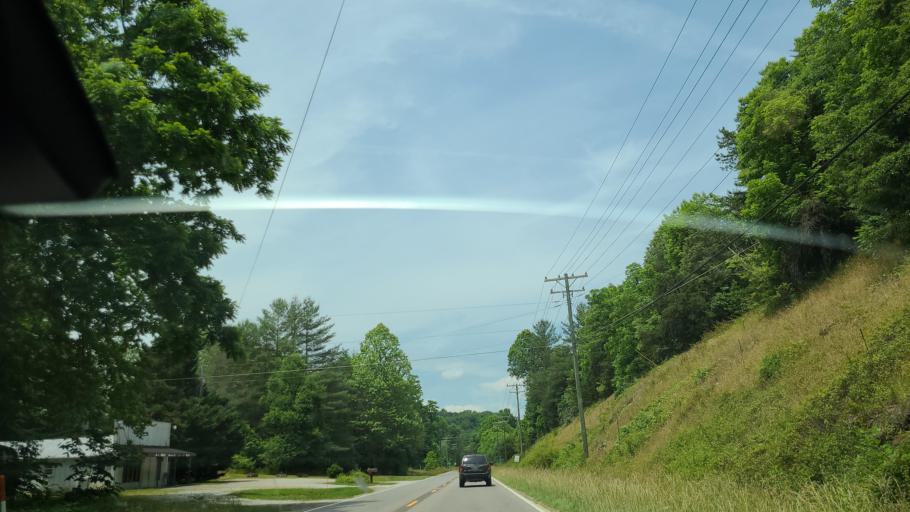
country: US
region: North Carolina
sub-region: Macon County
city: Franklin
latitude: 35.1660
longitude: -83.3276
